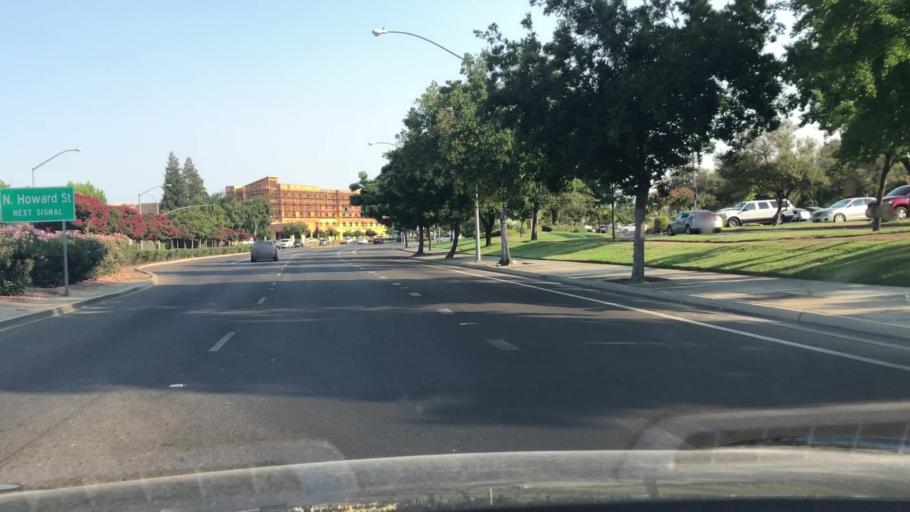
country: US
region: California
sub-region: Fresno County
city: Clovis
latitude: 36.8410
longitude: -119.7822
